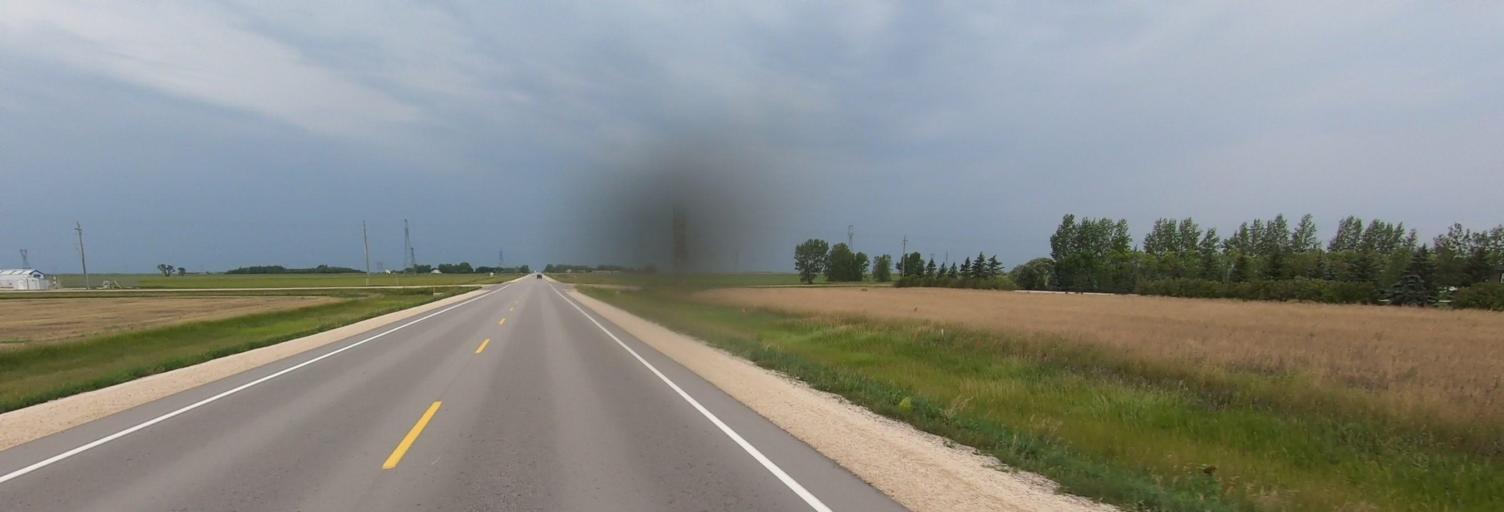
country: CA
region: Manitoba
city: Headingley
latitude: 49.7684
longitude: -97.3428
